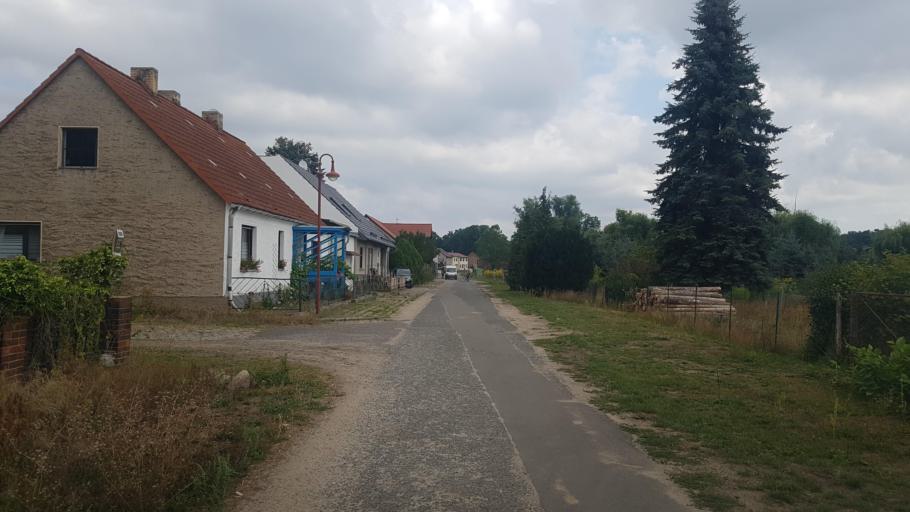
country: DE
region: Brandenburg
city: Belzig
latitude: 52.1710
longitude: 12.6727
